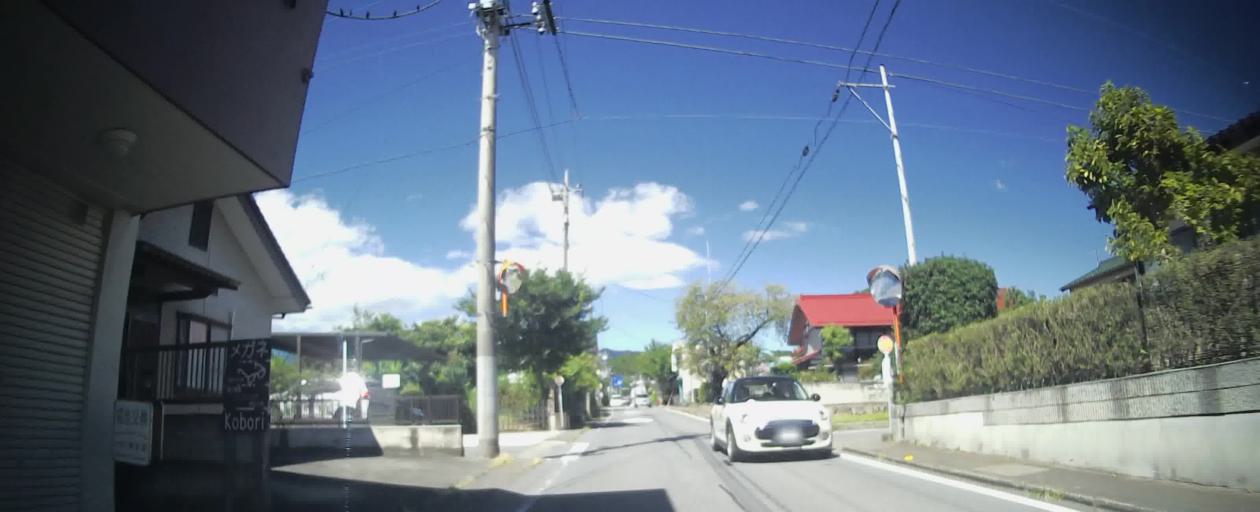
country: JP
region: Gunma
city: Kanekomachi
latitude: 36.3960
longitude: 138.9555
